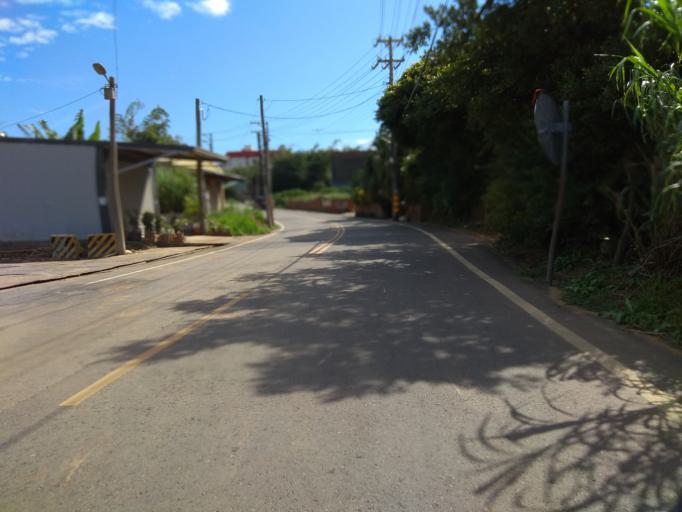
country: TW
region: Taiwan
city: Taoyuan City
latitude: 25.0394
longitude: 121.1273
